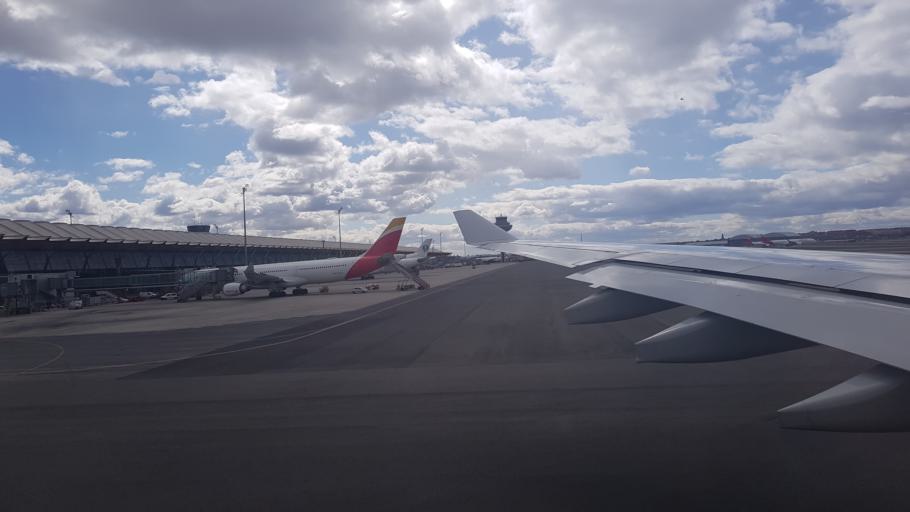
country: ES
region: Madrid
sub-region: Provincia de Madrid
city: Barajas de Madrid
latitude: 40.5003
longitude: -3.5696
